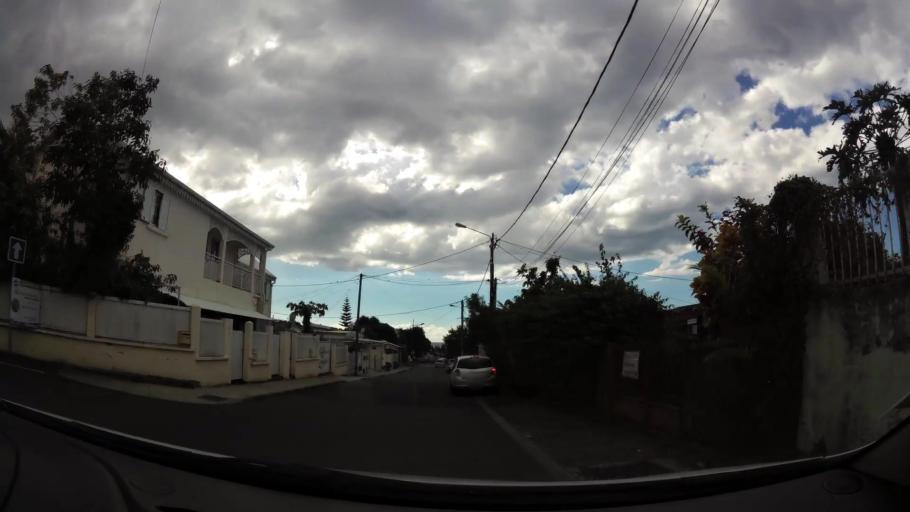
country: RE
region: Reunion
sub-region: Reunion
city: Saint-Denis
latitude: -20.8892
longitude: 55.4743
